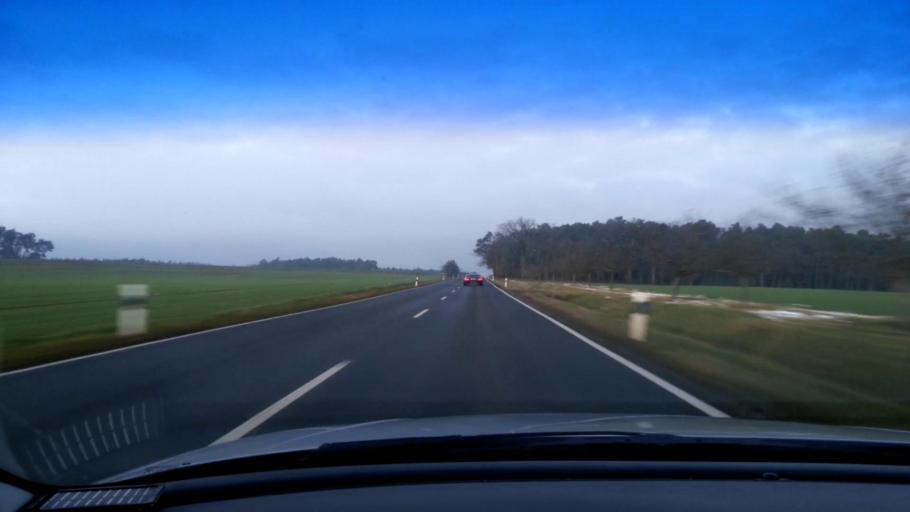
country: DE
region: Bavaria
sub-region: Upper Franconia
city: Pommersfelden
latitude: 49.7925
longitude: 10.8260
